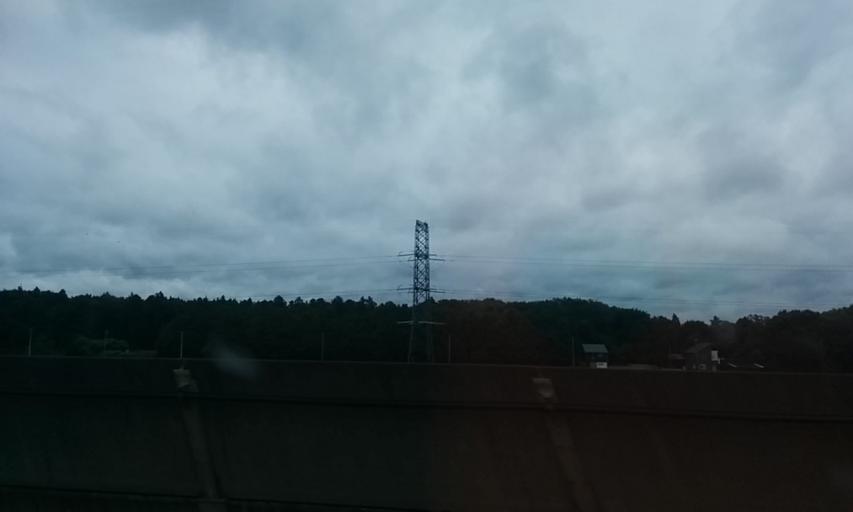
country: JP
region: Ibaraki
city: Koga
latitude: 36.2318
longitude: 139.7596
